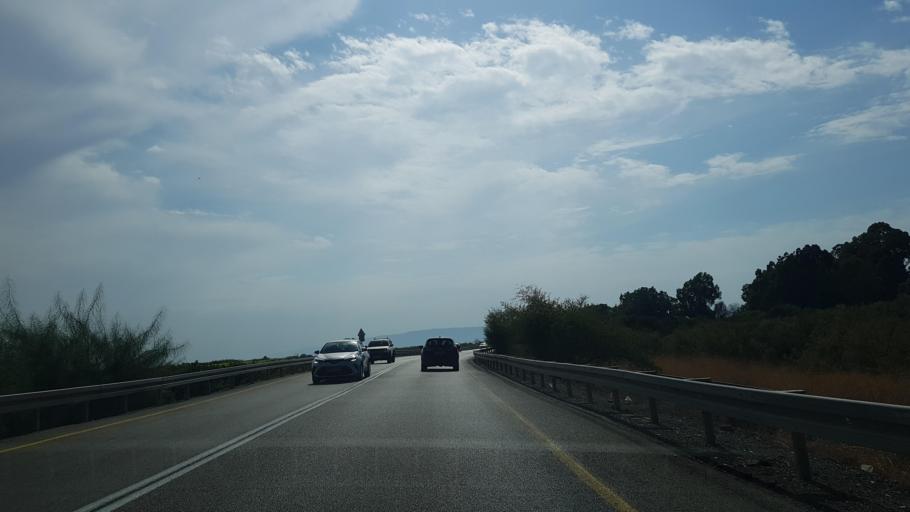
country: SY
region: Quneitra
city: Al Butayhah
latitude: 32.9039
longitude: 35.6176
